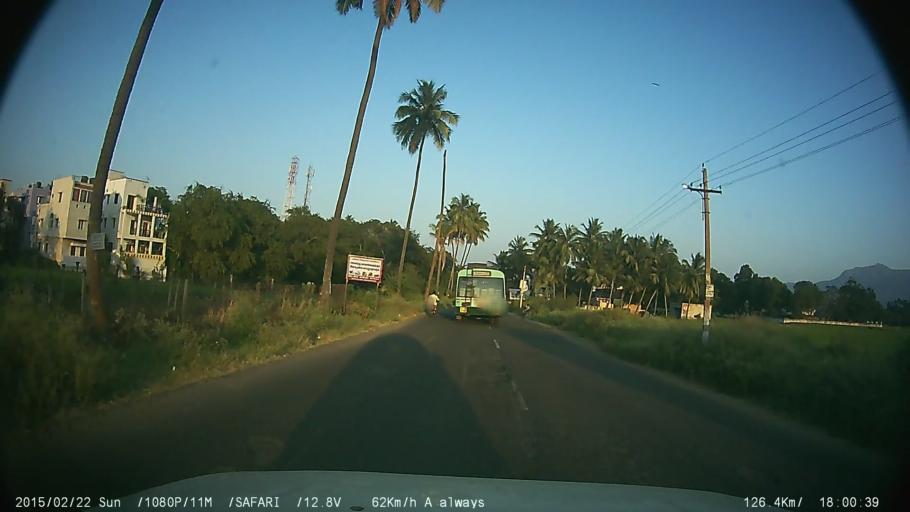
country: IN
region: Tamil Nadu
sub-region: Theni
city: Uttamapalaiyam
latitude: 9.8041
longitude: 77.3334
